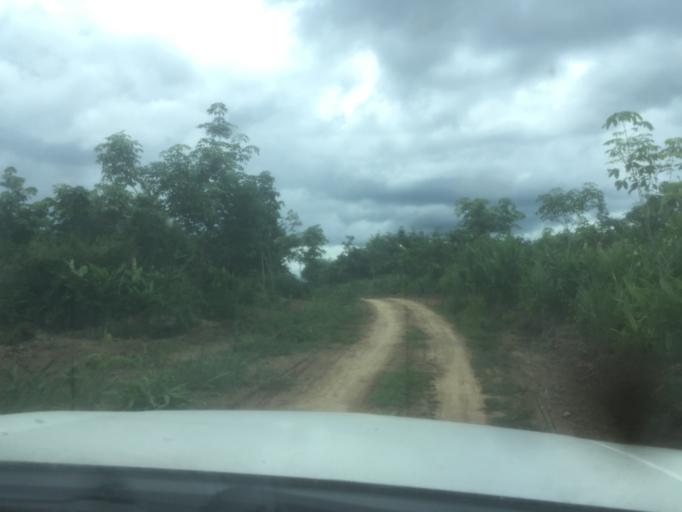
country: LA
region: Phongsali
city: Khoa
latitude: 20.9258
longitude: 102.5456
